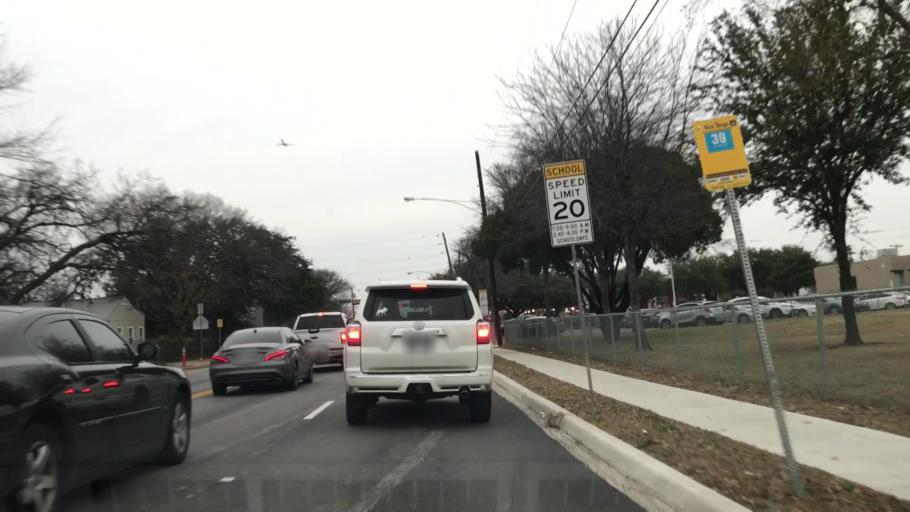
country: US
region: Texas
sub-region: Dallas County
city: University Park
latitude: 32.8249
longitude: -96.8300
